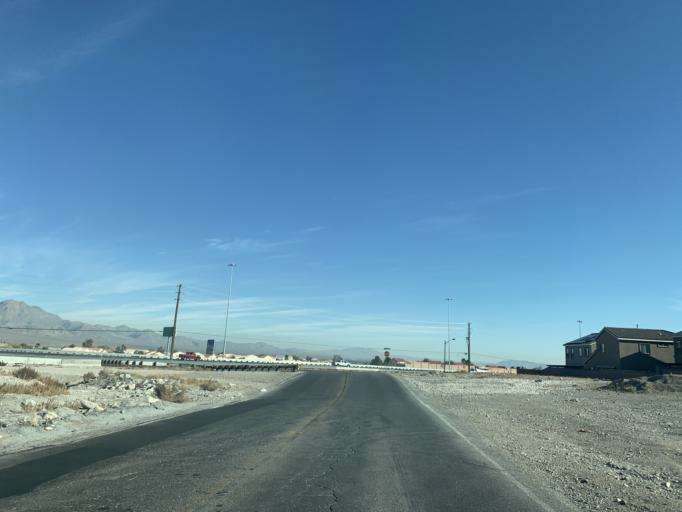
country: US
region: Nevada
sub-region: Clark County
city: Summerlin South
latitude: 36.3066
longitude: -115.2955
